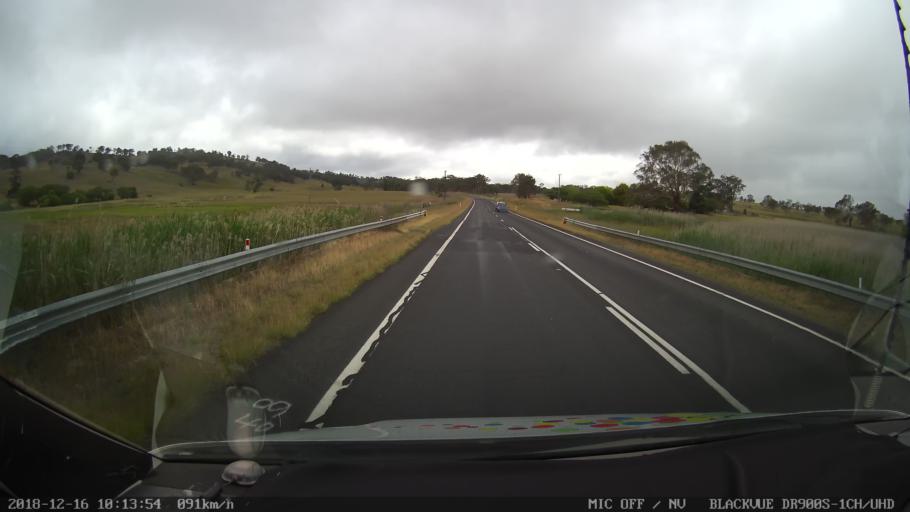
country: AU
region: New South Wales
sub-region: Tenterfield Municipality
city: Carrolls Creek
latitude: -29.2927
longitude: 151.9579
